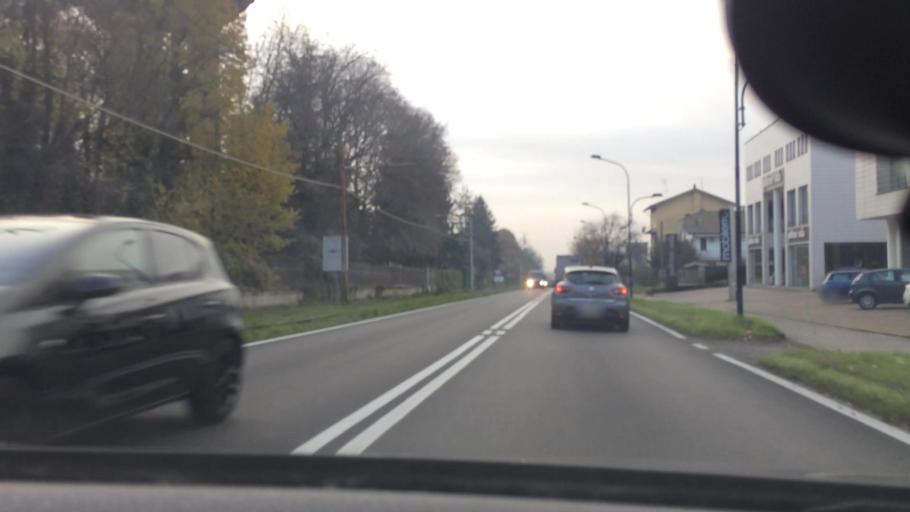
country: IT
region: Lombardy
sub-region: Provincia di Monza e Brianza
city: Villaggio del Sole
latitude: 45.6132
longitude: 9.1209
